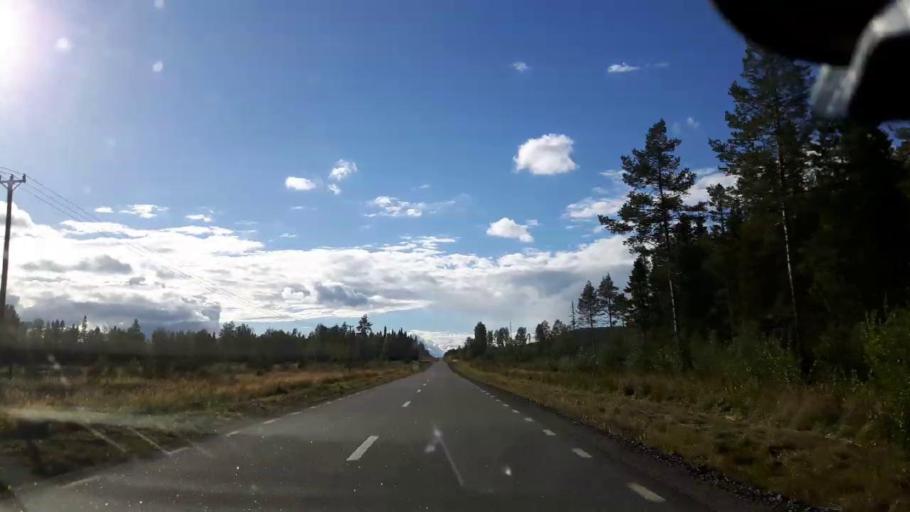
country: SE
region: Jaemtland
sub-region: Stroemsunds Kommun
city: Stroemsund
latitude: 63.5412
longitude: 15.9596
